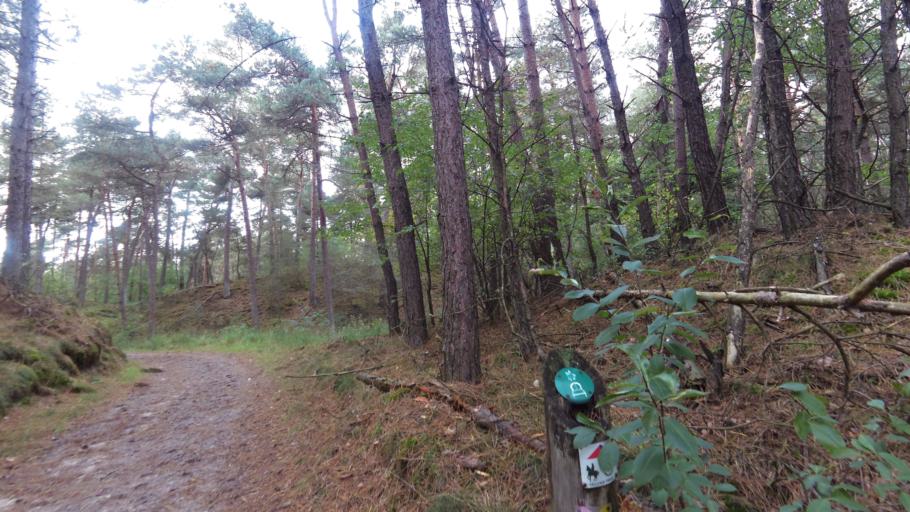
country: NL
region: Gelderland
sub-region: Gemeente Ede
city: Harskamp
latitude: 52.1589
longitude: 5.7606
